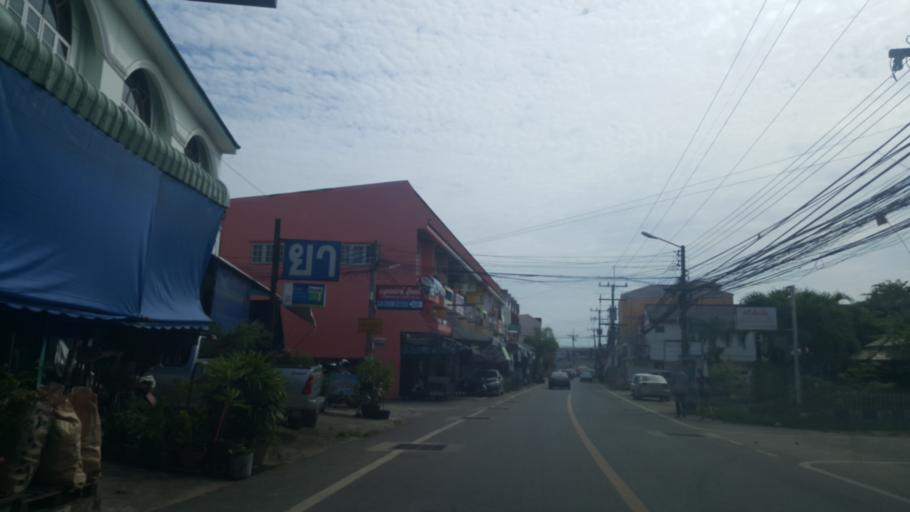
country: TH
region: Chon Buri
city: Sattahip
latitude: 12.6757
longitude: 100.9031
